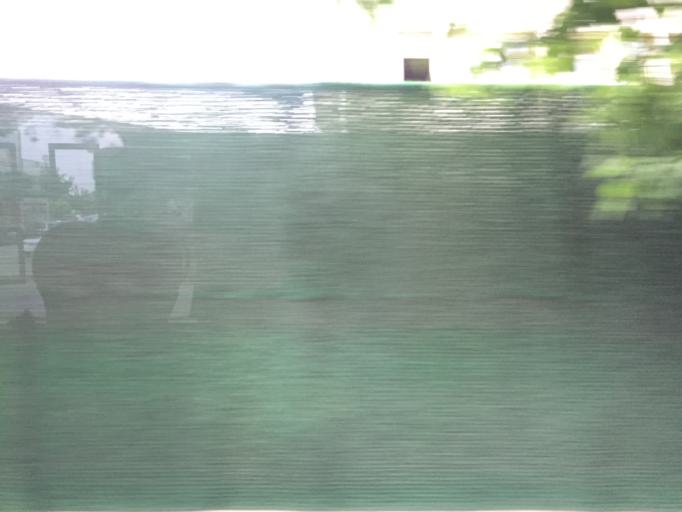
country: TR
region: Gaziantep
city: Gaziantep
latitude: 37.0674
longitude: 37.3744
